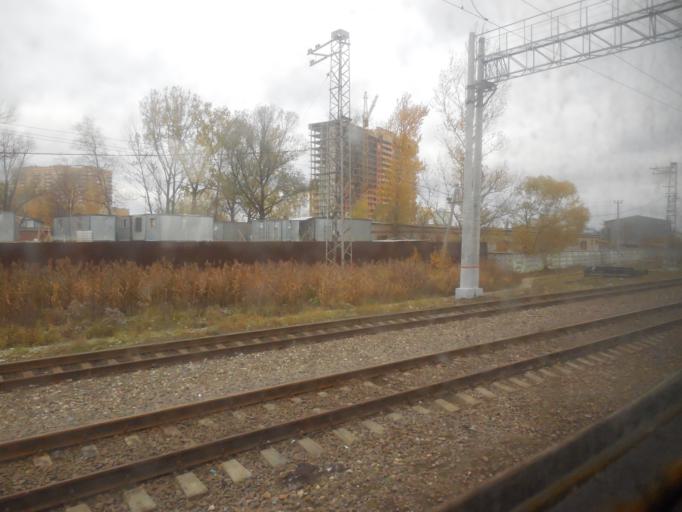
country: RU
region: Moskovskaya
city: Golitsyno
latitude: 55.6141
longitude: 36.9786
